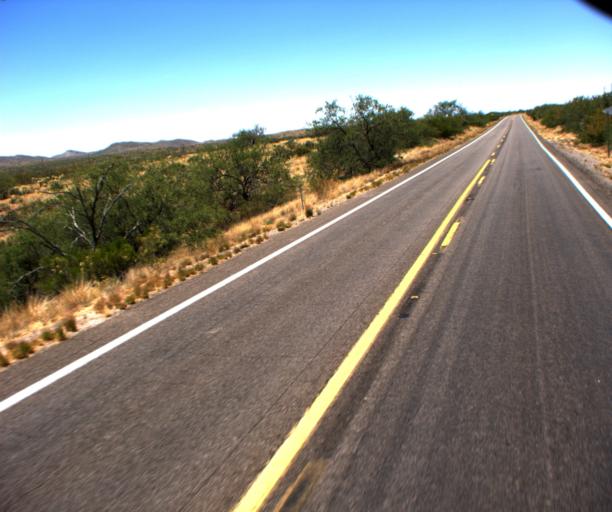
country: US
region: Arizona
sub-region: Pima County
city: Catalina
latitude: 32.5888
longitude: -110.9655
